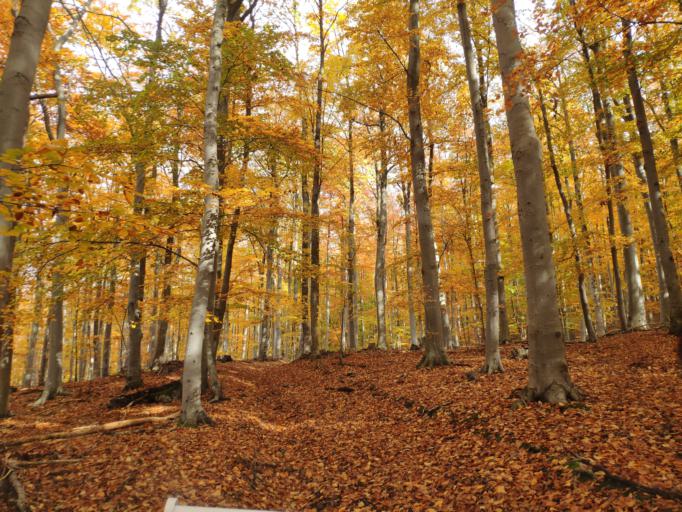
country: SK
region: Kosicky
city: Medzev
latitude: 48.7303
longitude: 20.9863
